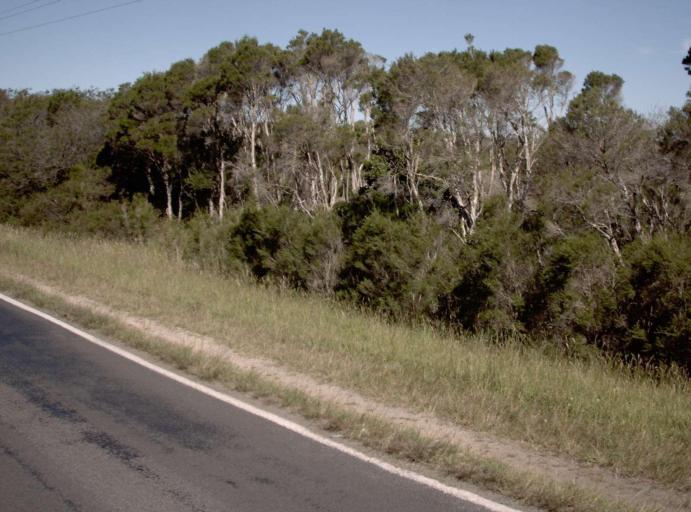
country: AU
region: Victoria
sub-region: Latrobe
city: Morwell
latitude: -38.6344
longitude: 146.5401
